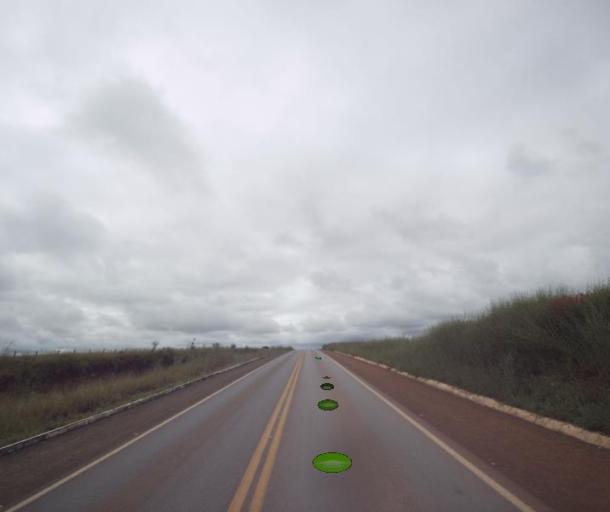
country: BR
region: Goias
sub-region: Uruacu
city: Uruacu
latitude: -14.6892
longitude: -49.1239
